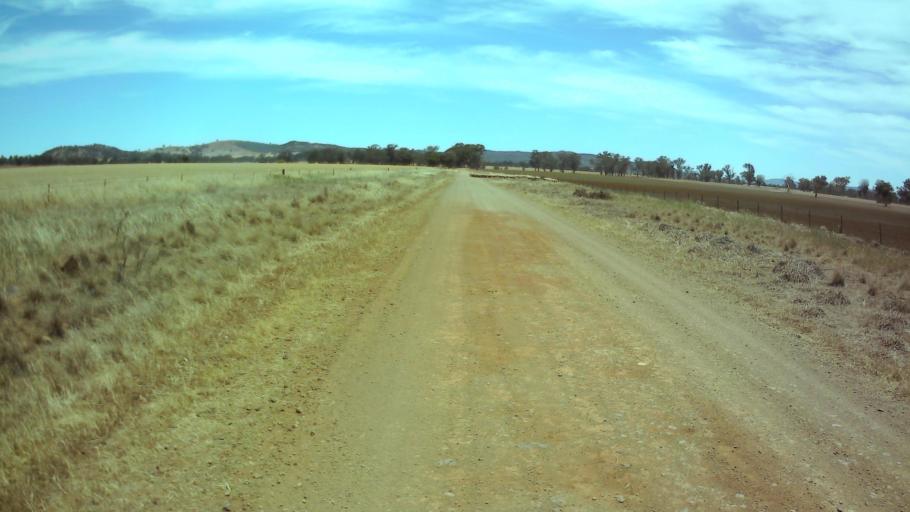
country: AU
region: New South Wales
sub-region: Weddin
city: Grenfell
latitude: -33.7506
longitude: 148.1444
